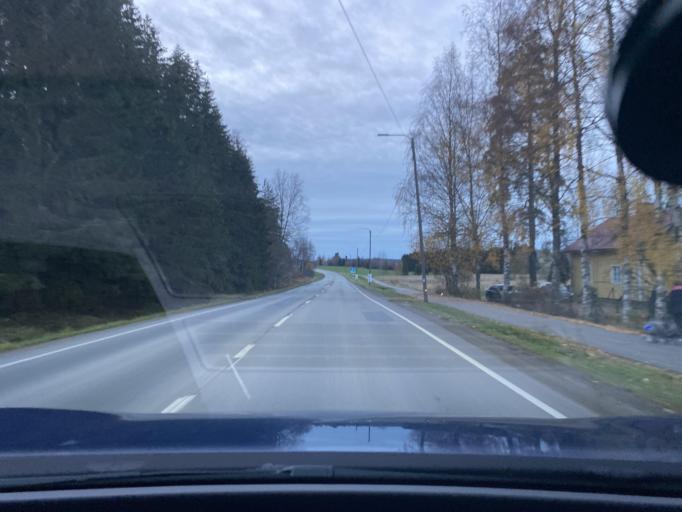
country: FI
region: Uusimaa
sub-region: Helsinki
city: Saukkola
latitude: 60.3807
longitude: 23.9551
